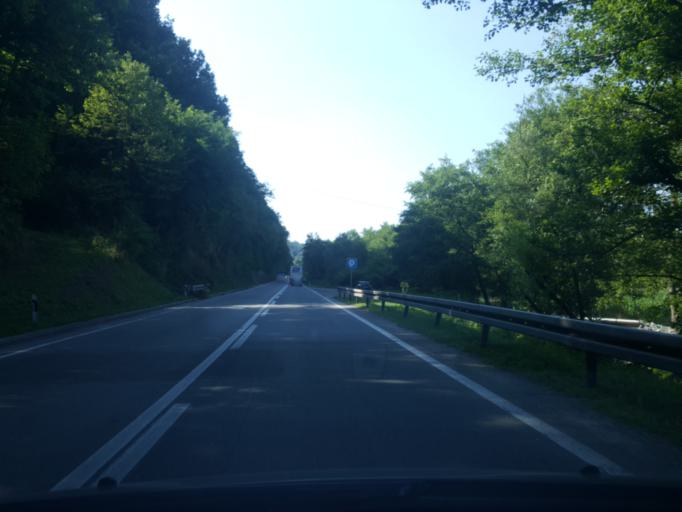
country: RS
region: Central Serbia
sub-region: Moravicki Okrug
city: Gornji Milanovac
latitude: 44.0781
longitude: 20.4856
